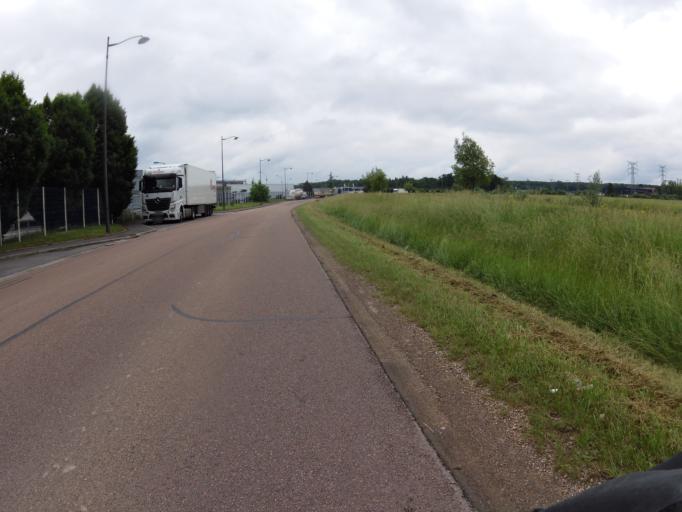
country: FR
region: Champagne-Ardenne
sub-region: Departement de la Haute-Marne
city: Saint-Dizier
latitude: 48.6504
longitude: 4.9345
